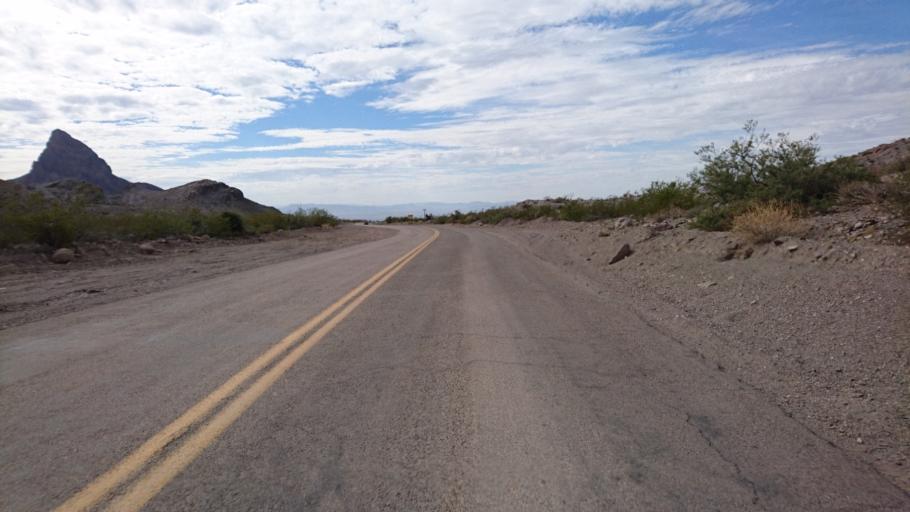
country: US
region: Arizona
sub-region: Mohave County
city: Mohave Valley
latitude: 35.0050
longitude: -114.3978
